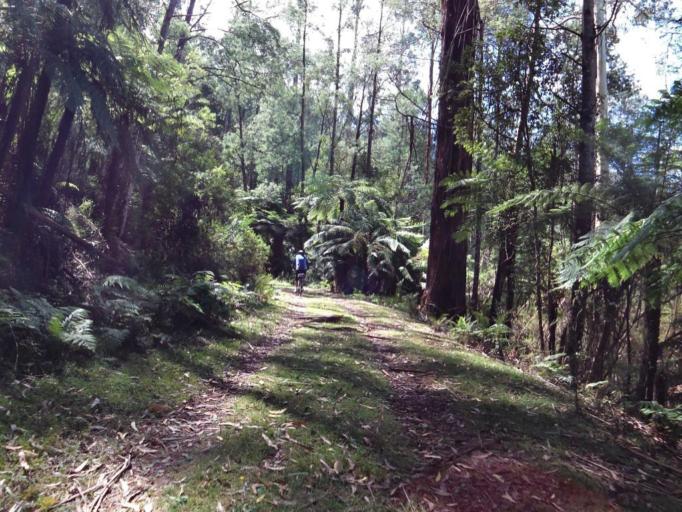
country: AU
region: Victoria
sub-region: Yarra Ranges
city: Millgrove
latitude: -37.6904
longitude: 145.8045
